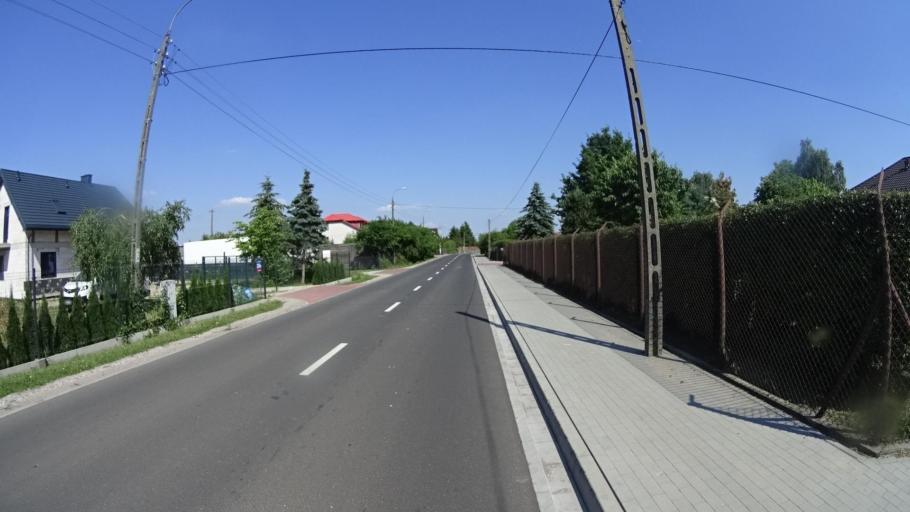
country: PL
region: Masovian Voivodeship
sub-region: Powiat warszawski zachodni
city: Blonie
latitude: 52.1693
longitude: 20.6173
